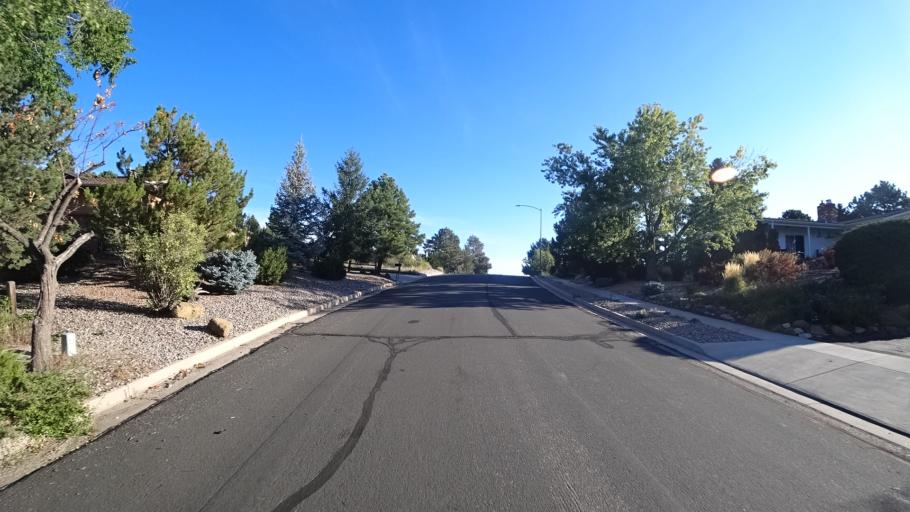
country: US
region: Colorado
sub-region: El Paso County
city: Cimarron Hills
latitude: 38.8873
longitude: -104.7679
